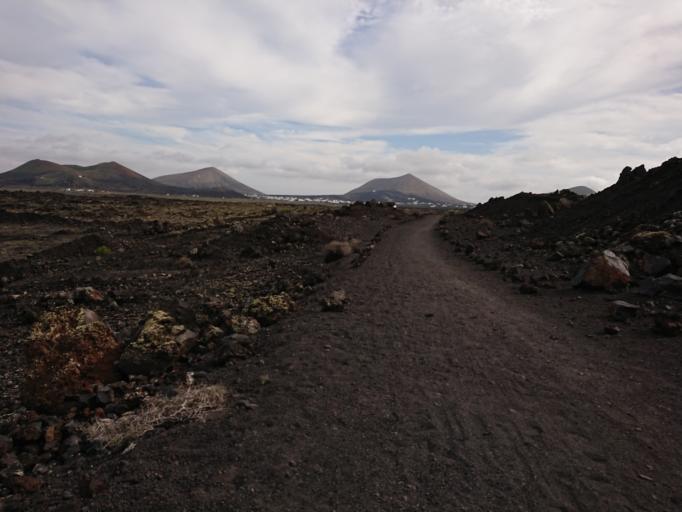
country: ES
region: Canary Islands
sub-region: Provincia de Las Palmas
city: Tinajo
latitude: 29.0087
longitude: -13.6764
